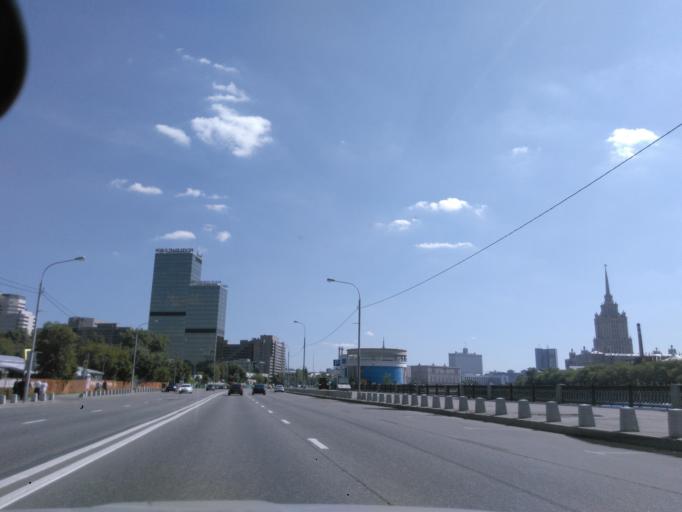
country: RU
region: Moskovskaya
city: Presnenskiy
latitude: 55.7507
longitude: 37.5500
